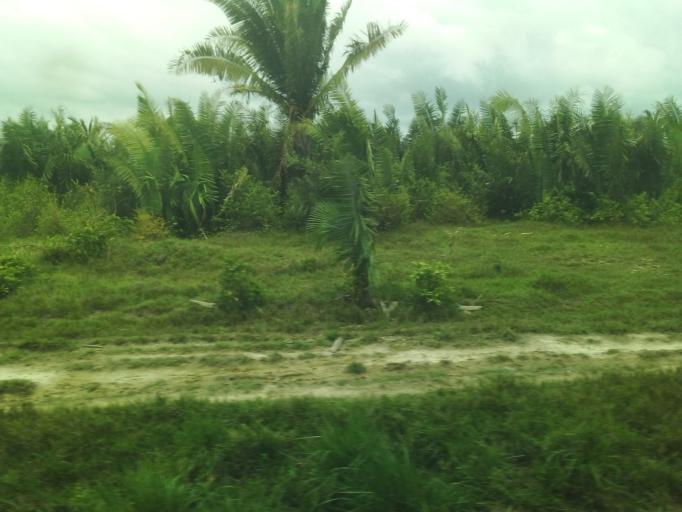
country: BR
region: Maranhao
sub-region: Moncao
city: Moncao
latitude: -3.5829
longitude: -45.0674
